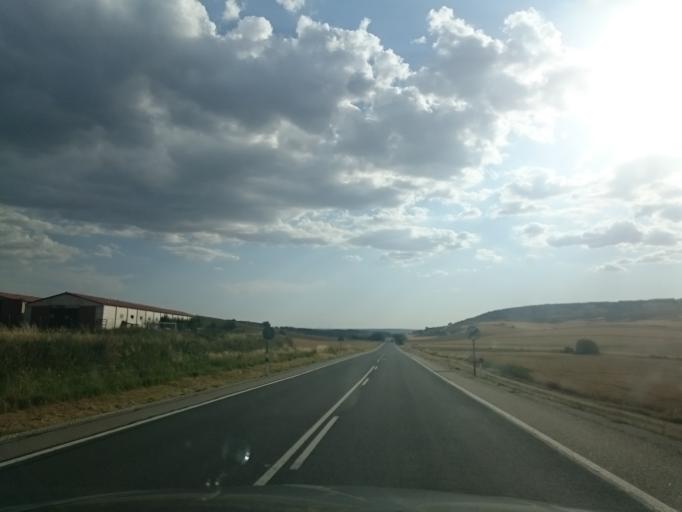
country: ES
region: Castille and Leon
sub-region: Provincia de Burgos
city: Atapuerca
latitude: 42.3458
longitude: -3.4892
